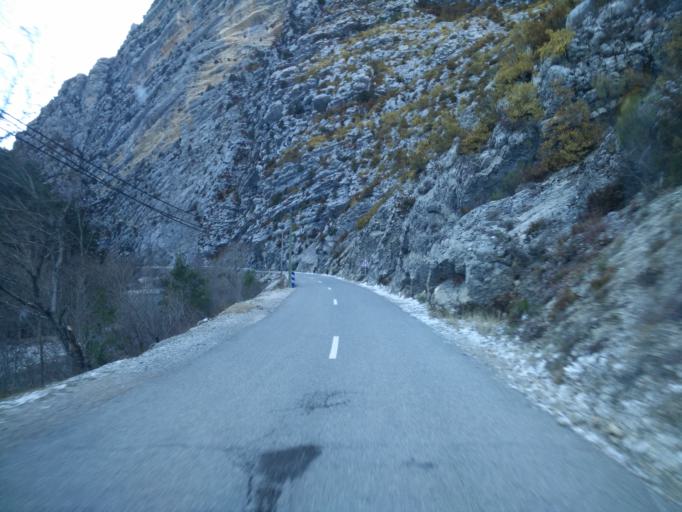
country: FR
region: Provence-Alpes-Cote d'Azur
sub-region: Departement des Alpes-de-Haute-Provence
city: Castellane
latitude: 43.8319
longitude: 6.4490
